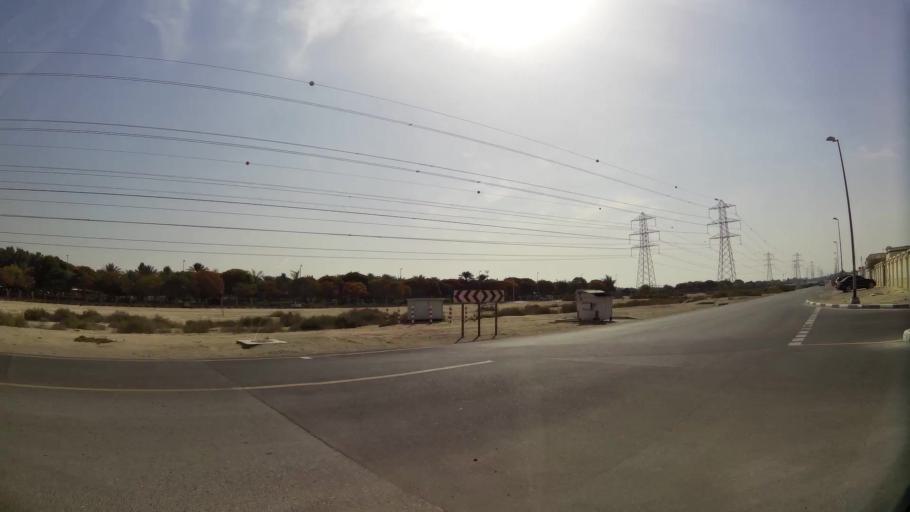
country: AE
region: Ash Shariqah
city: Sharjah
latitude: 25.2677
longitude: 55.3974
